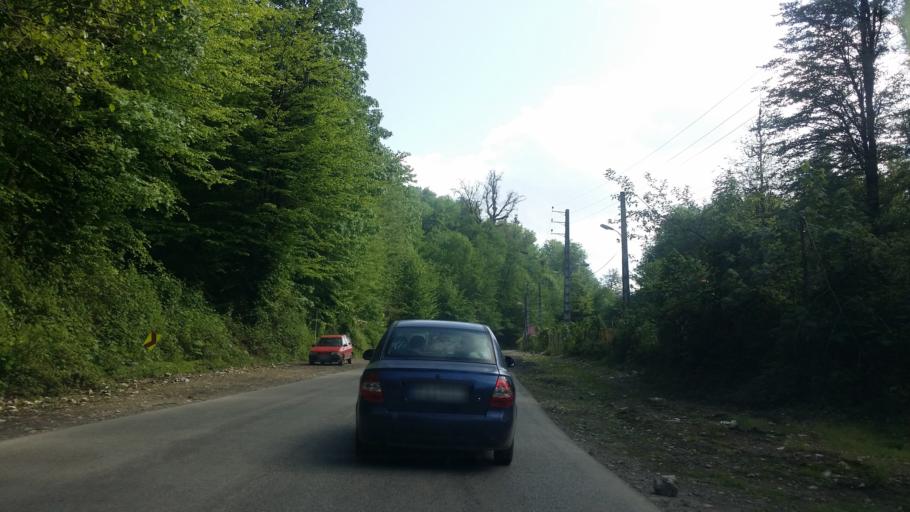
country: IR
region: Mazandaran
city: `Abbasabad
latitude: 36.6532
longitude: 51.1120
